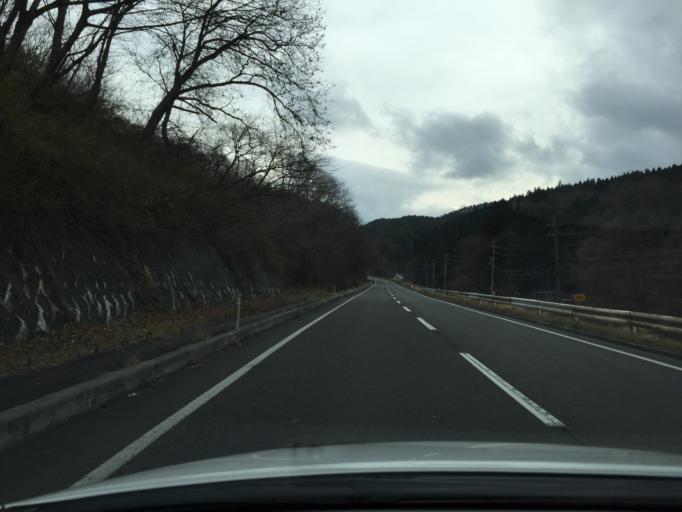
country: JP
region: Fukushima
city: Ishikawa
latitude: 37.1801
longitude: 140.6491
